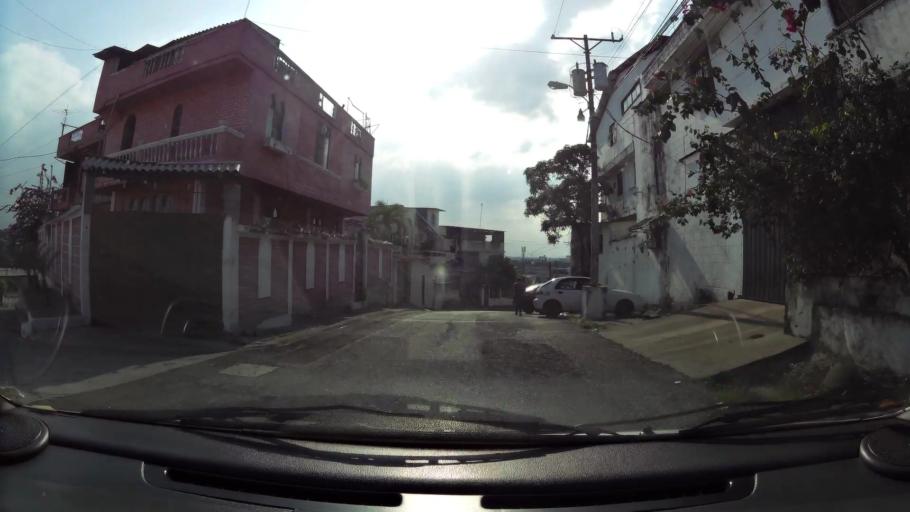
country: EC
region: Guayas
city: Guayaquil
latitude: -2.1545
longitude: -79.9085
